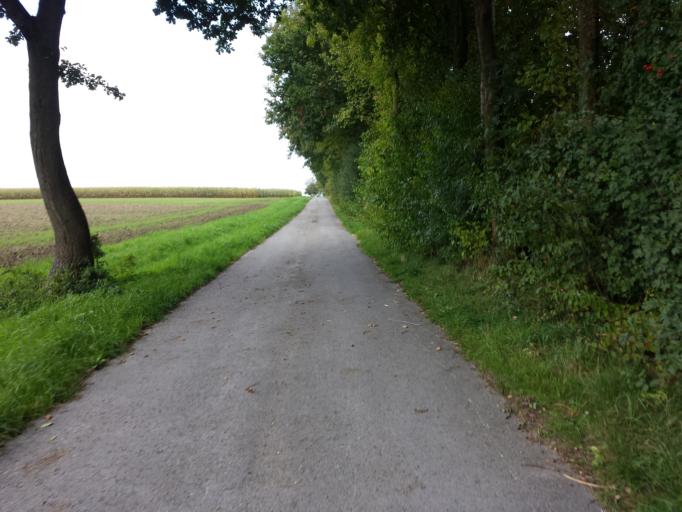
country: DE
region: North Rhine-Westphalia
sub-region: Regierungsbezirk Detmold
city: Langenberg
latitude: 51.7818
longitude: 8.3060
